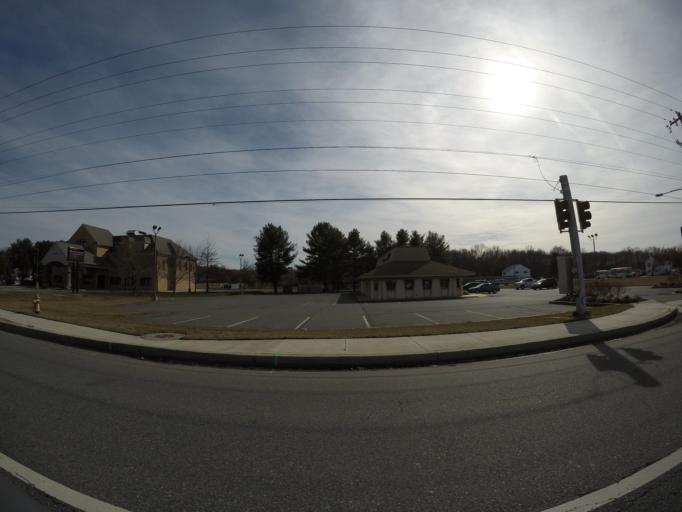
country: US
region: Maryland
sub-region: Cecil County
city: Elkton
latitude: 39.5982
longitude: -75.8148
